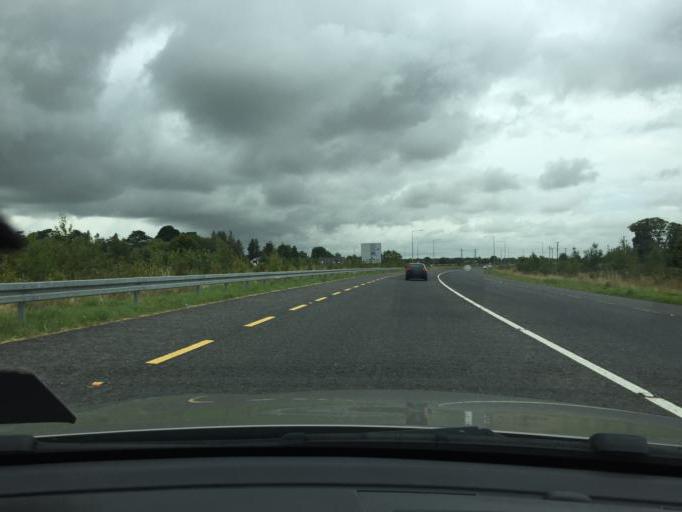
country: IE
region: Leinster
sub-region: An Mhi
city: Dunboyne
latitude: 53.4224
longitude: -6.4902
